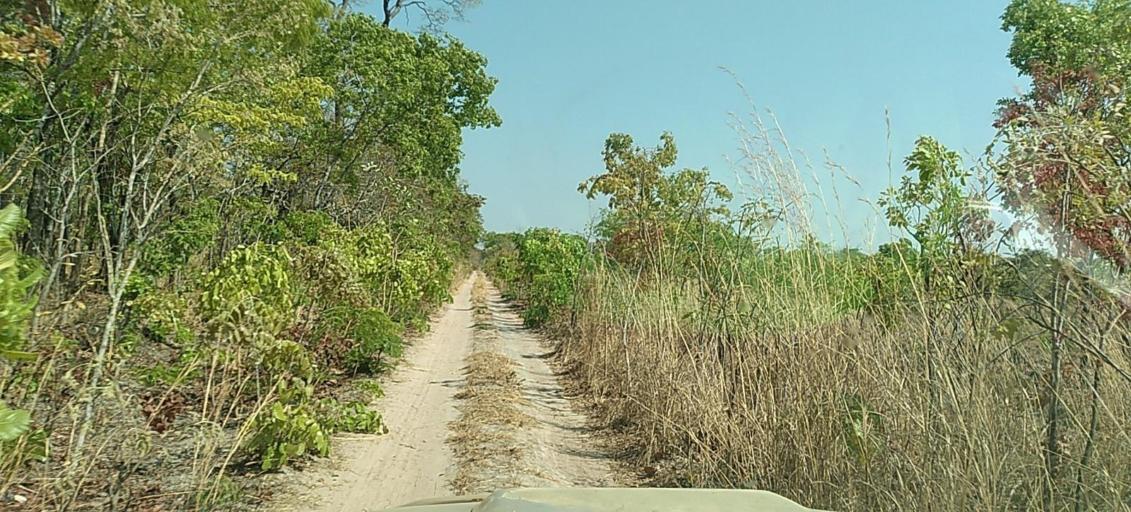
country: ZM
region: North-Western
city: Kalengwa
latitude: -13.3243
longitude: 24.8262
